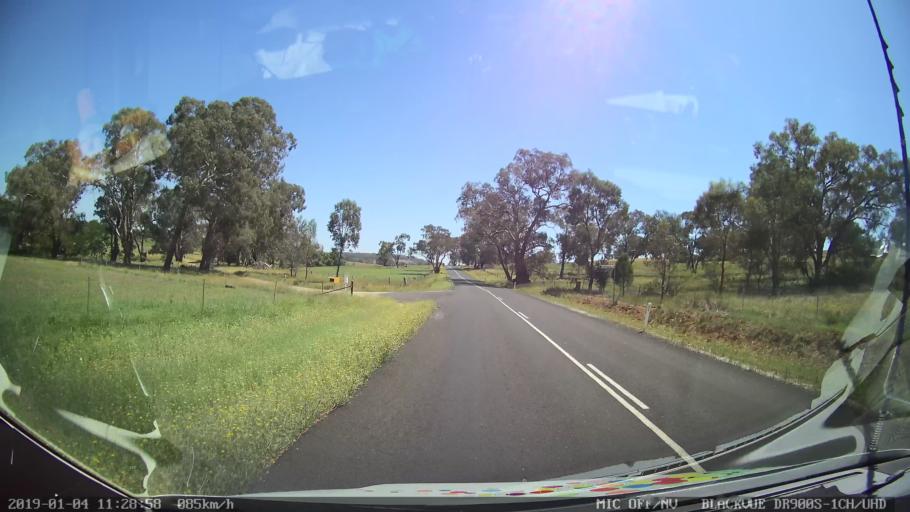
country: AU
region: New South Wales
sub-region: Cabonne
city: Molong
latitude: -33.0936
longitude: 148.7728
